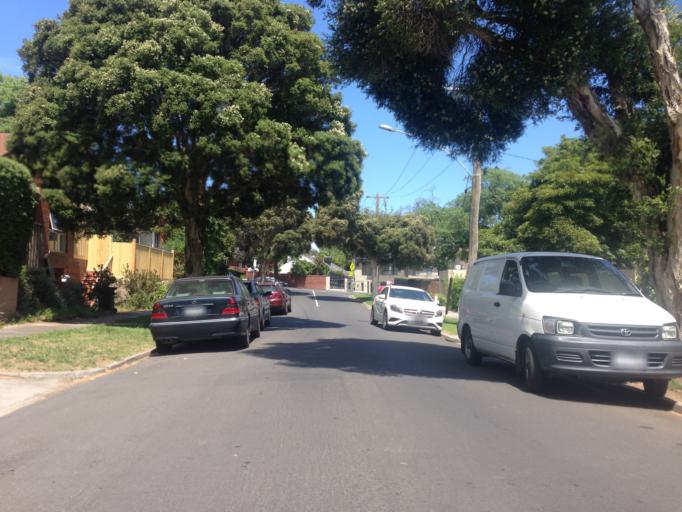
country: AU
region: Victoria
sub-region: Boroondara
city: Balwyn North
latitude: -37.7873
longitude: 145.0742
